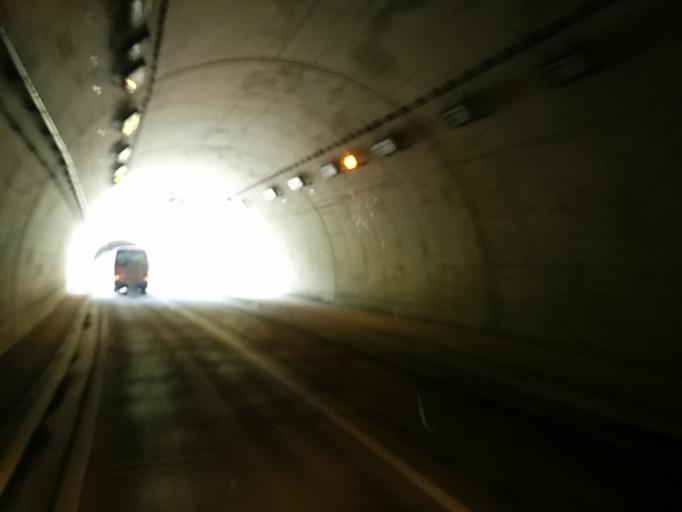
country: JP
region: Ehime
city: Niihama
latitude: 33.8887
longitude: 133.3069
